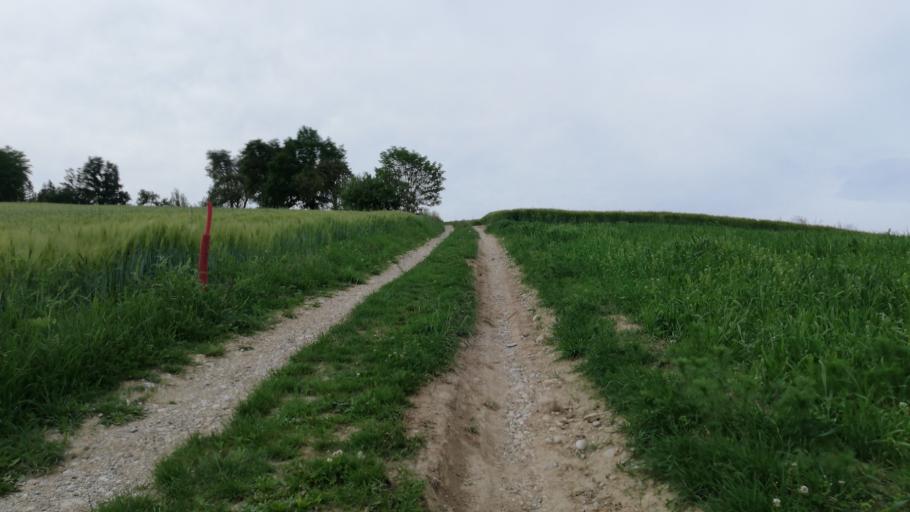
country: AT
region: Upper Austria
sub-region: Wels-Land
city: Gunskirchen
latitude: 48.1779
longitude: 13.9465
